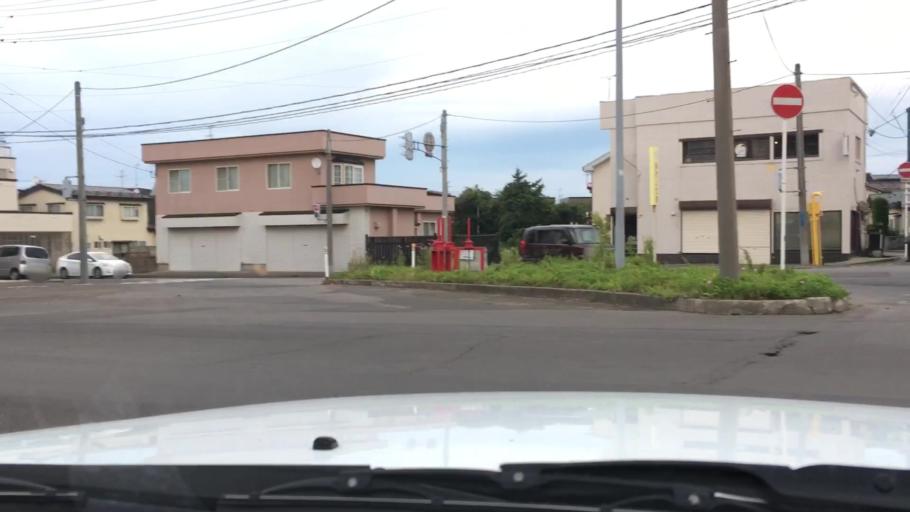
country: JP
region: Aomori
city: Hirosaki
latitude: 40.5848
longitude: 140.4750
